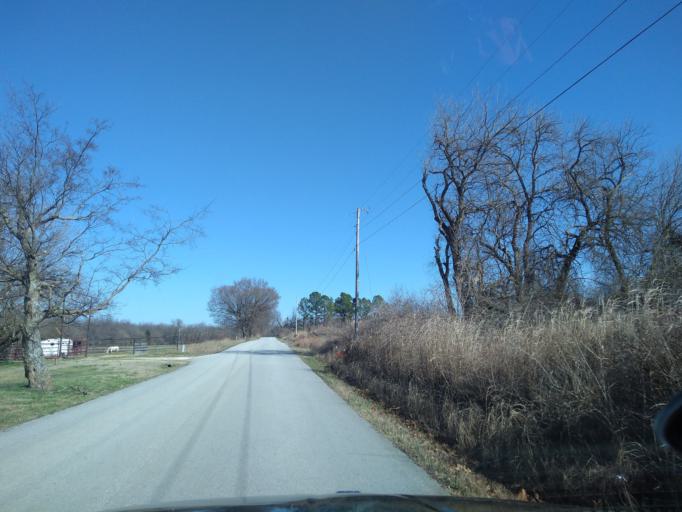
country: US
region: Arkansas
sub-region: Washington County
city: Farmington
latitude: 36.0610
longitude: -94.2451
